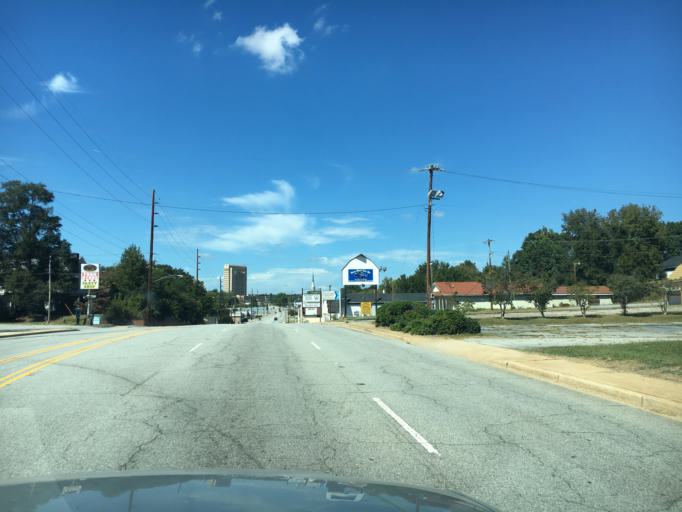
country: US
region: South Carolina
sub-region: Spartanburg County
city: Spartanburg
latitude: 34.9443
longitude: -81.9173
